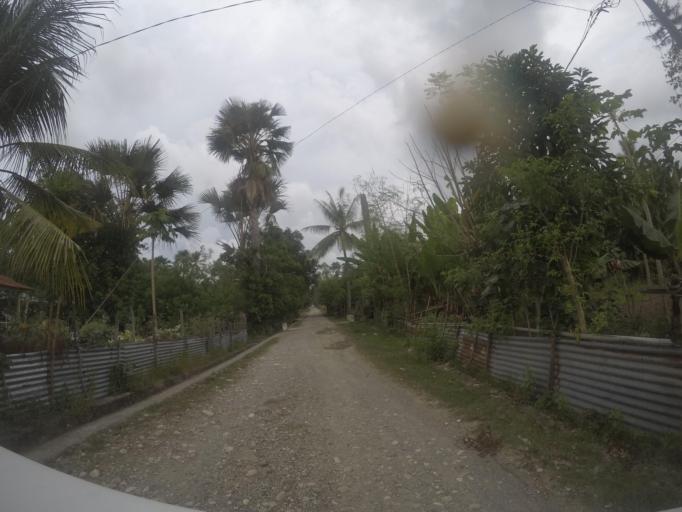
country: TL
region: Viqueque
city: Viqueque
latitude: -8.8789
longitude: 126.3665
